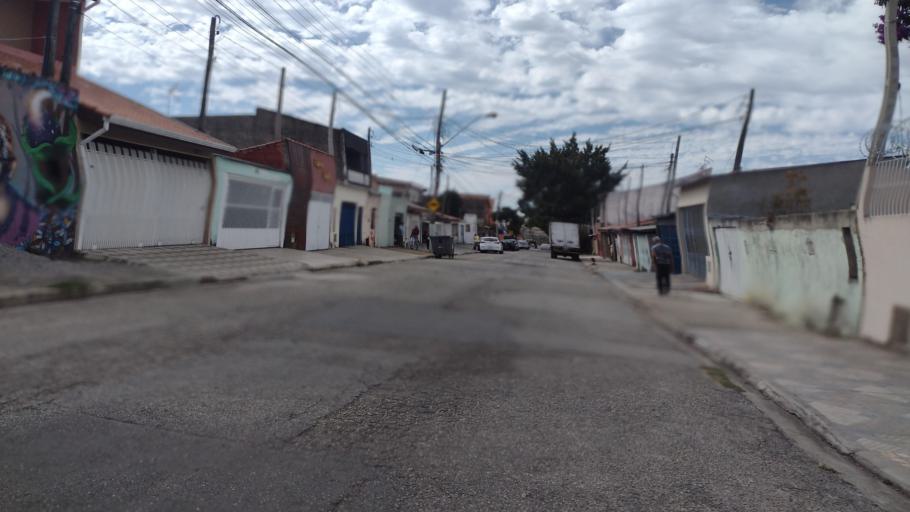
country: BR
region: Sao Paulo
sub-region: Sorocaba
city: Sorocaba
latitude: -23.4314
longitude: -47.4604
